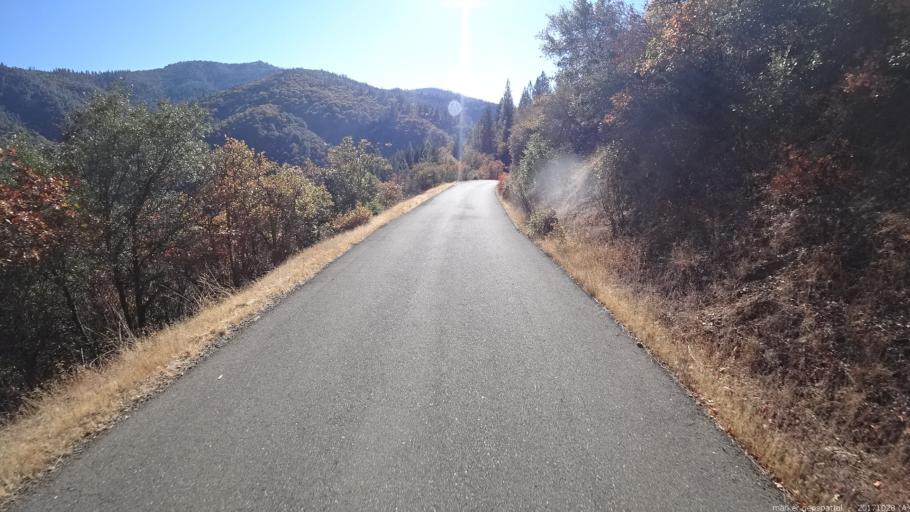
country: US
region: California
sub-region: Trinity County
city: Lewiston
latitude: 40.7991
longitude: -122.6125
